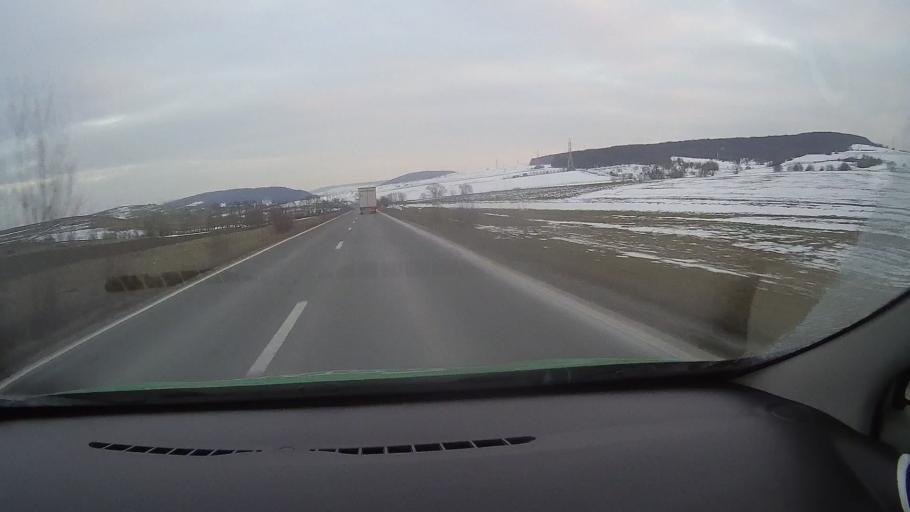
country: RO
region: Harghita
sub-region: Comuna Lupeni
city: Lupeni
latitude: 46.3560
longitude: 25.2523
